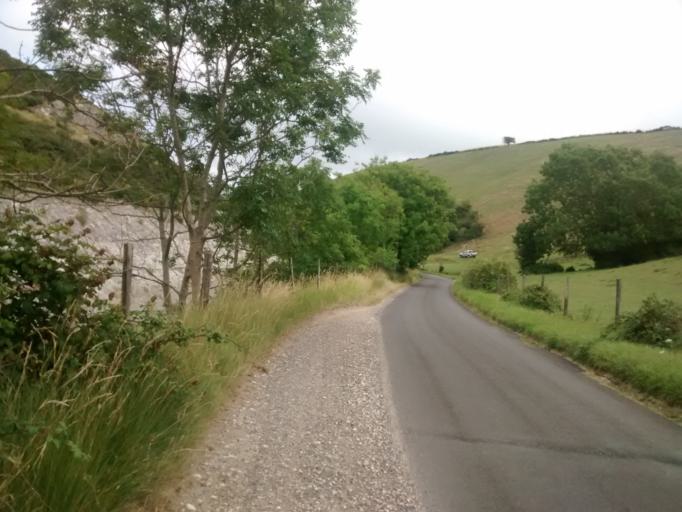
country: GB
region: England
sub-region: Dorset
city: Wareham
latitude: 50.6395
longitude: -2.0997
